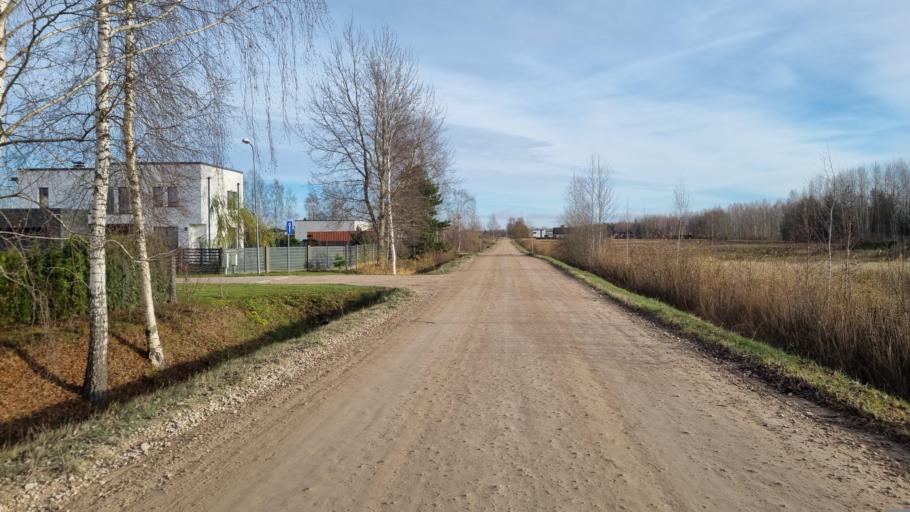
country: LV
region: Marupe
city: Marupe
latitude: 56.9089
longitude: 24.0087
